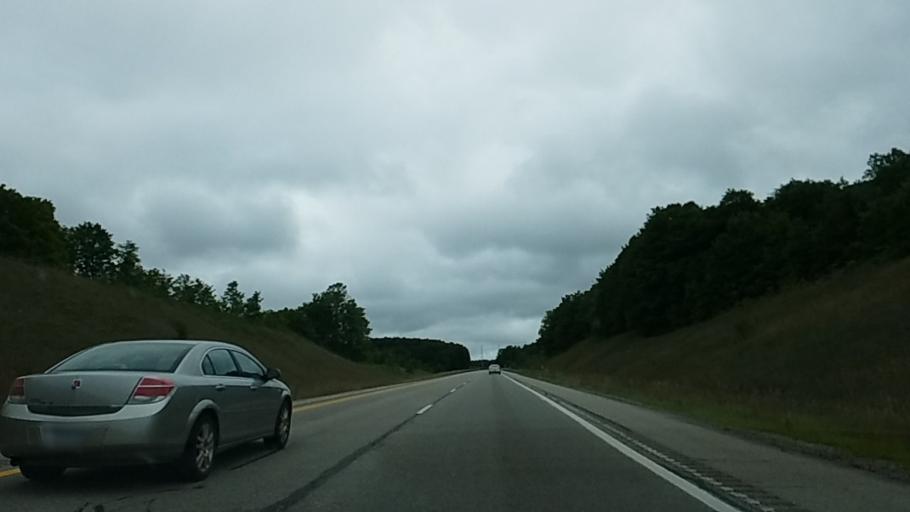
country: US
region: Michigan
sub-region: Otsego County
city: Gaylord
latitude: 45.1189
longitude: -84.6771
